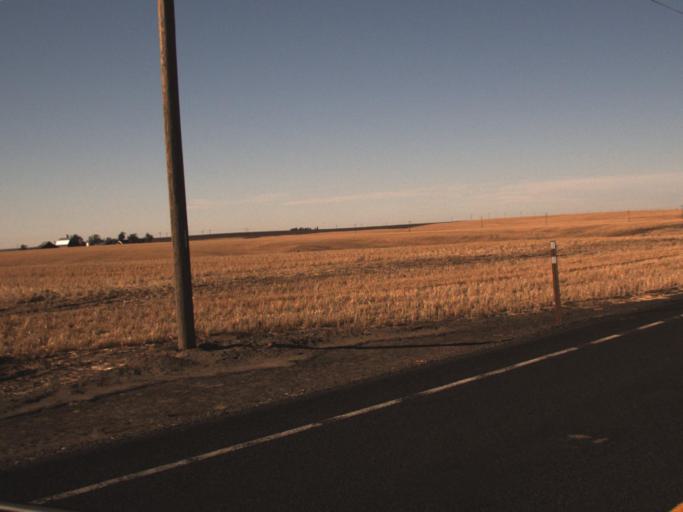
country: US
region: Washington
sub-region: Adams County
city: Ritzville
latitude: 46.9071
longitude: -118.3330
